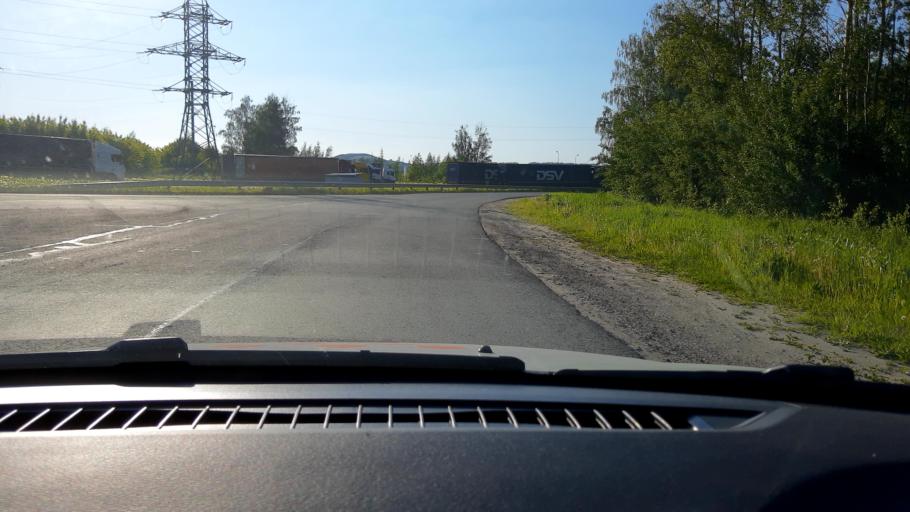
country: RU
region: Nizjnij Novgorod
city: Kstovo
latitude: 56.1048
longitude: 44.1282
